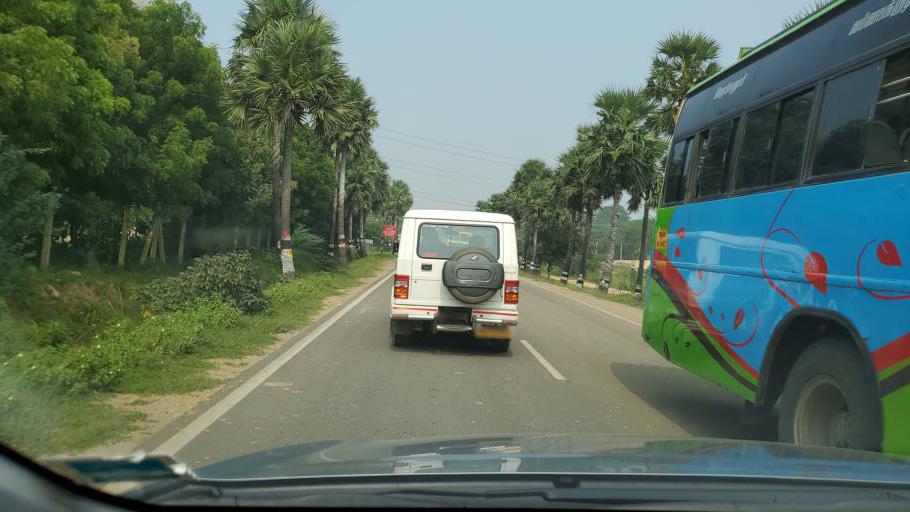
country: IN
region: Tamil Nadu
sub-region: Ariyalur
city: Ariyalur
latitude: 11.1197
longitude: 79.1482
